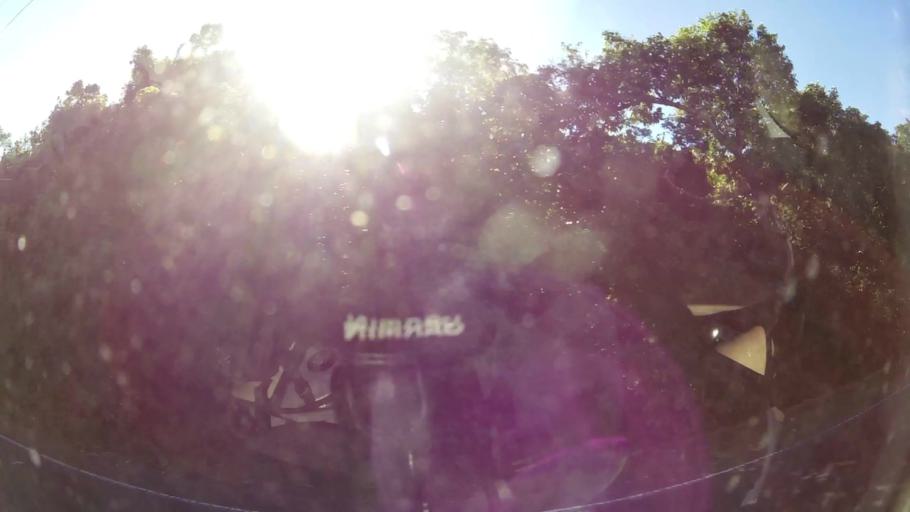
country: SV
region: Sonsonate
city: Juayua
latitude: 13.8539
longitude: -89.7734
